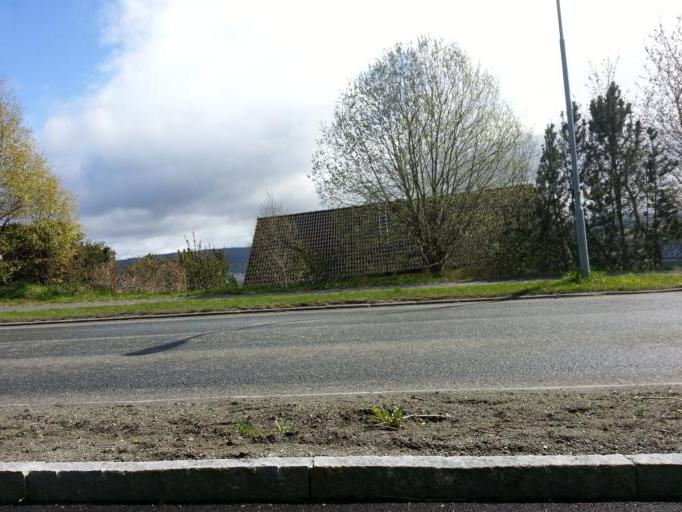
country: NO
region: Sor-Trondelag
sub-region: Trondheim
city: Trondheim
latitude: 63.3909
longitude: 10.3683
